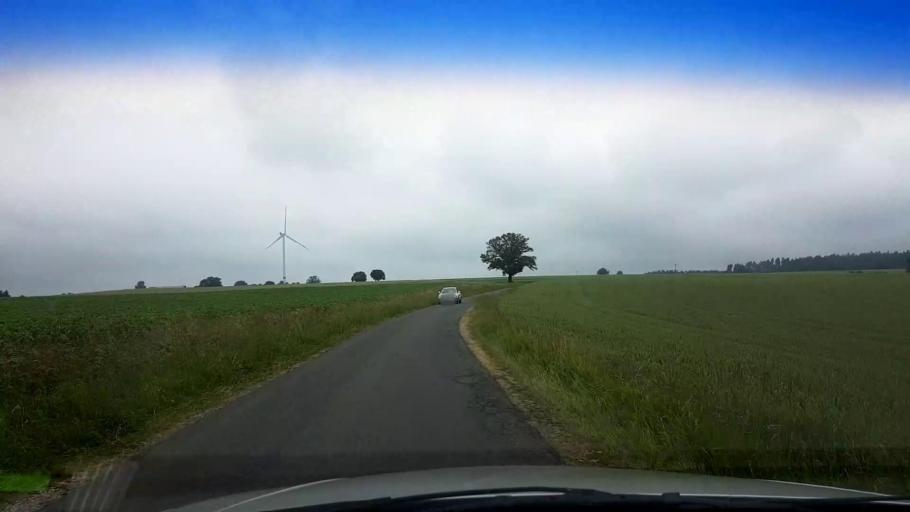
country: DE
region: Bavaria
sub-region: Upper Franconia
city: Thiersheim
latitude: 50.0816
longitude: 12.1414
